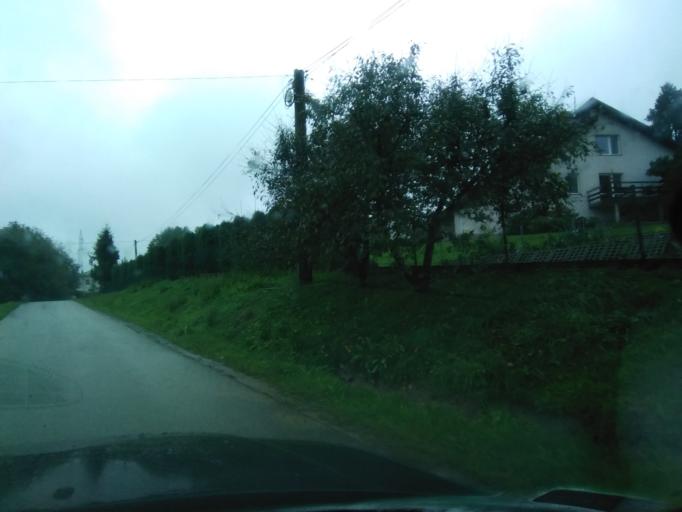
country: PL
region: Subcarpathian Voivodeship
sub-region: Powiat ropczycko-sedziszowski
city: Niedzwiada
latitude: 50.0262
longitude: 21.5411
